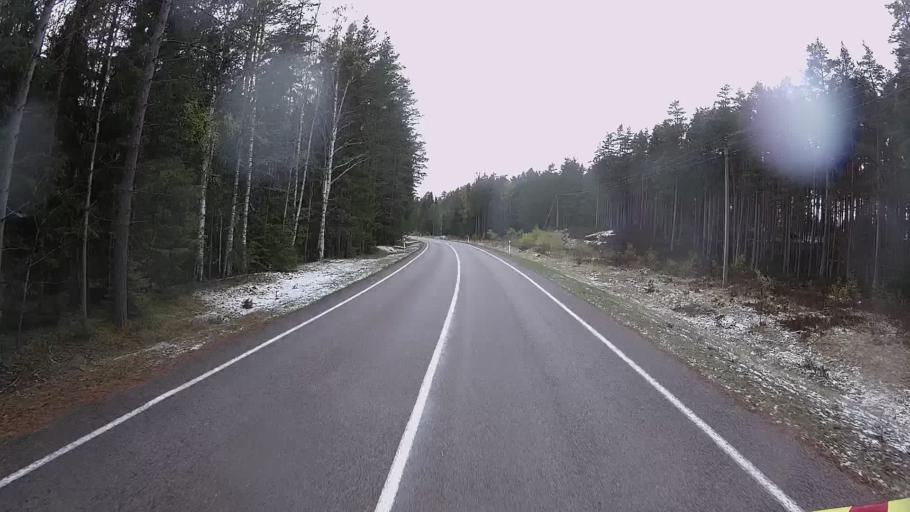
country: EE
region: Hiiumaa
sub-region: Kaerdla linn
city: Kardla
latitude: 58.8897
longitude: 22.4348
